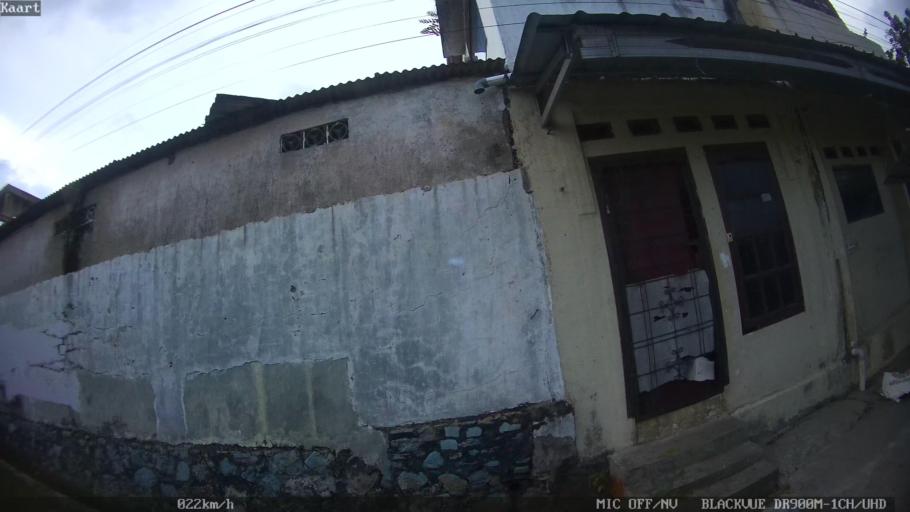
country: ID
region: Lampung
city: Kedaton
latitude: -5.3978
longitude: 105.2108
